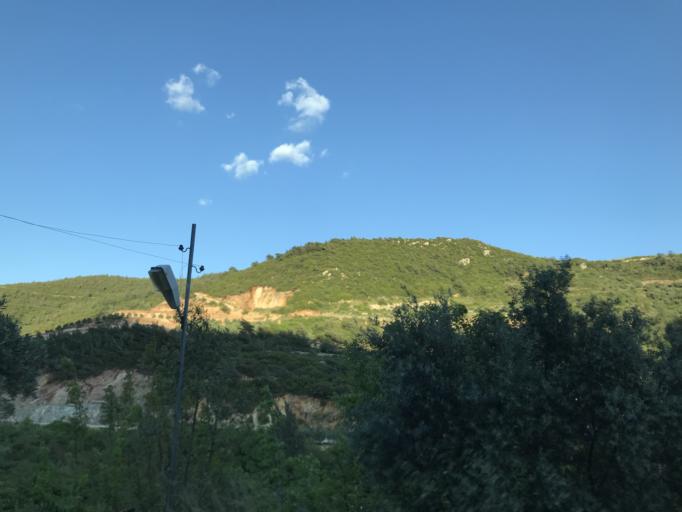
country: TR
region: Hatay
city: Buyukcat
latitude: 36.0827
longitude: 36.0501
